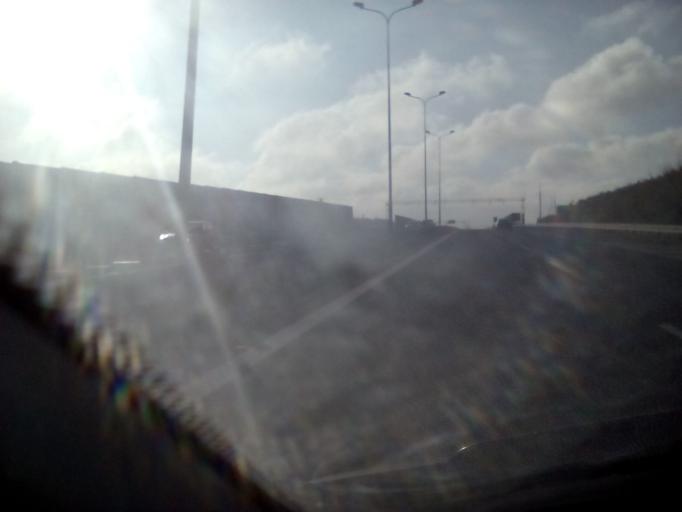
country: PL
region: Masovian Voivodeship
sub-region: Powiat grojecki
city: Goszczyn
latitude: 51.7564
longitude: 20.9058
